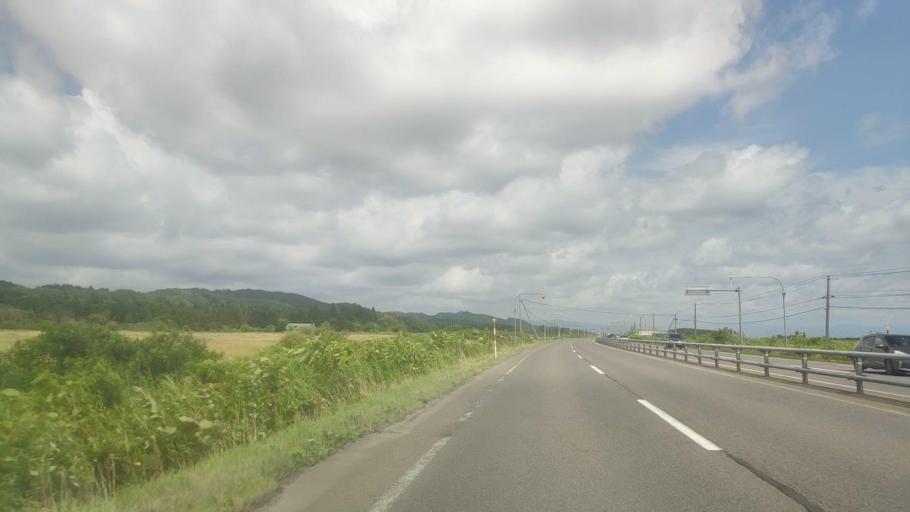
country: JP
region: Hokkaido
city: Niseko Town
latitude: 42.4098
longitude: 140.3065
